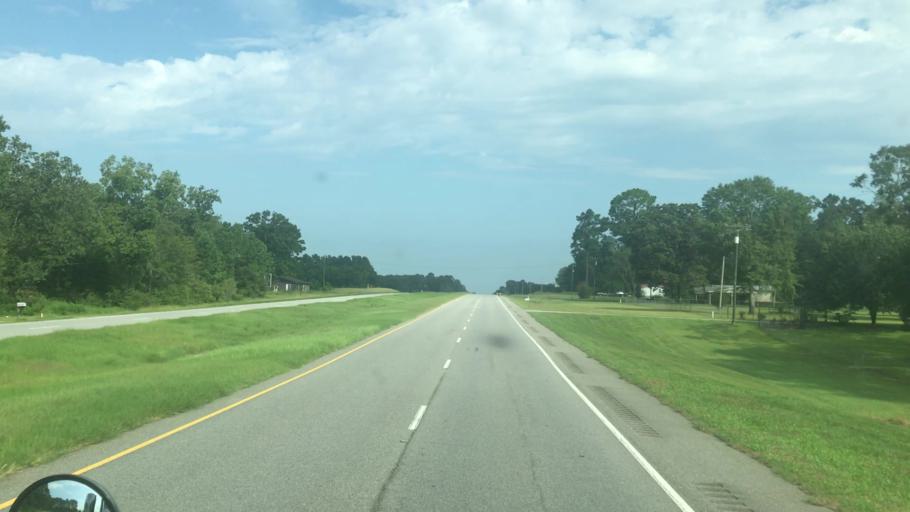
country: US
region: Georgia
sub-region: Early County
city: Blakely
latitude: 31.3112
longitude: -84.8718
